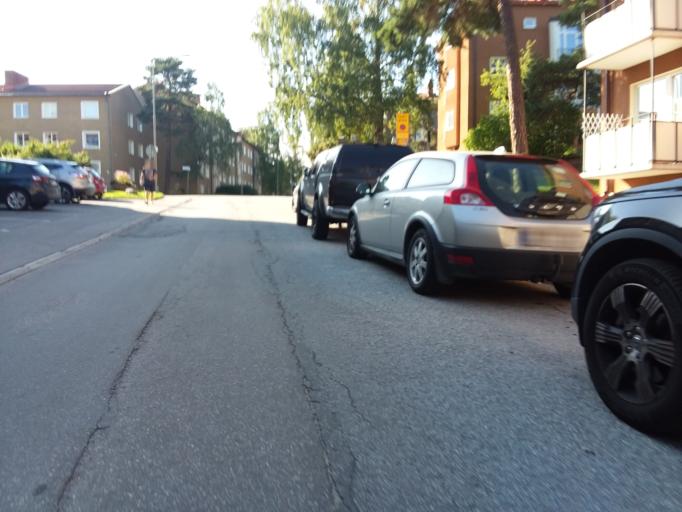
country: SE
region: Stockholm
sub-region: Stockholms Kommun
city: Bromma
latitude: 59.3464
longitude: 17.8885
